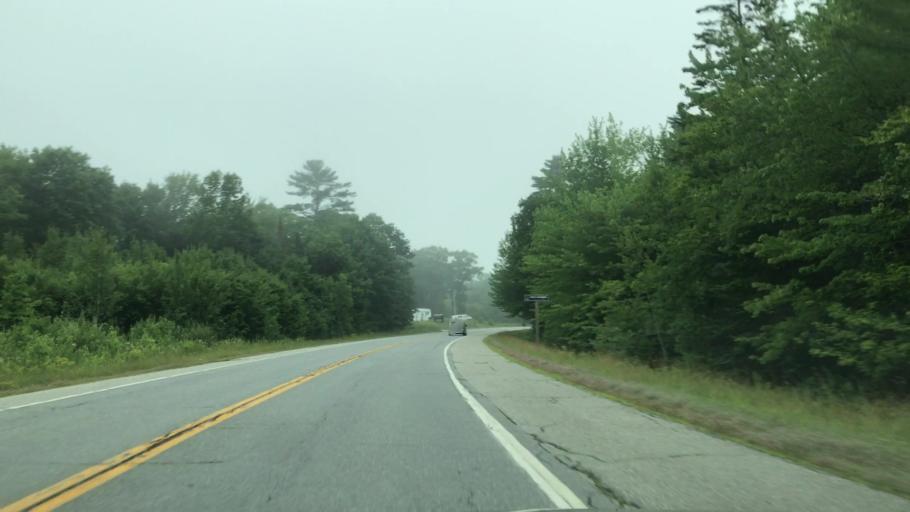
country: US
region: Maine
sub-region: Knox County
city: Warren
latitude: 44.1621
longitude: -69.1781
